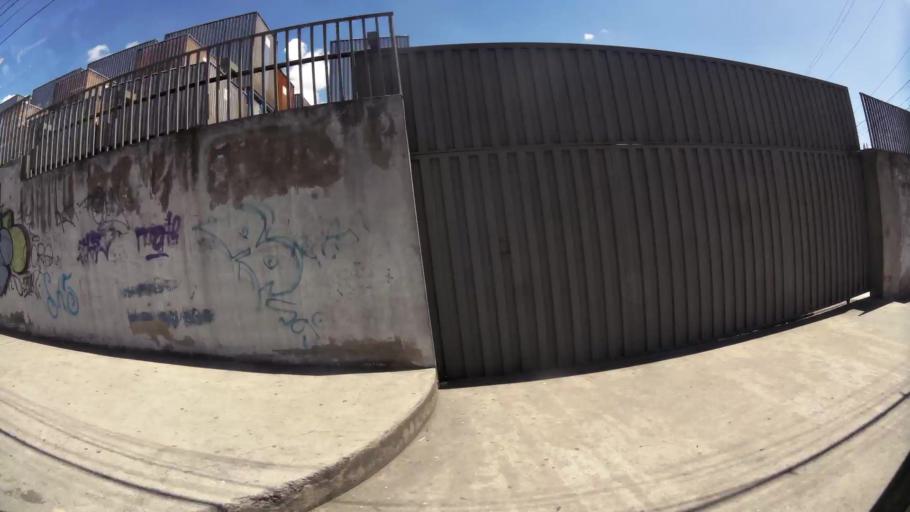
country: EC
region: Pichincha
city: Quito
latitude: -0.1011
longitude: -78.4726
